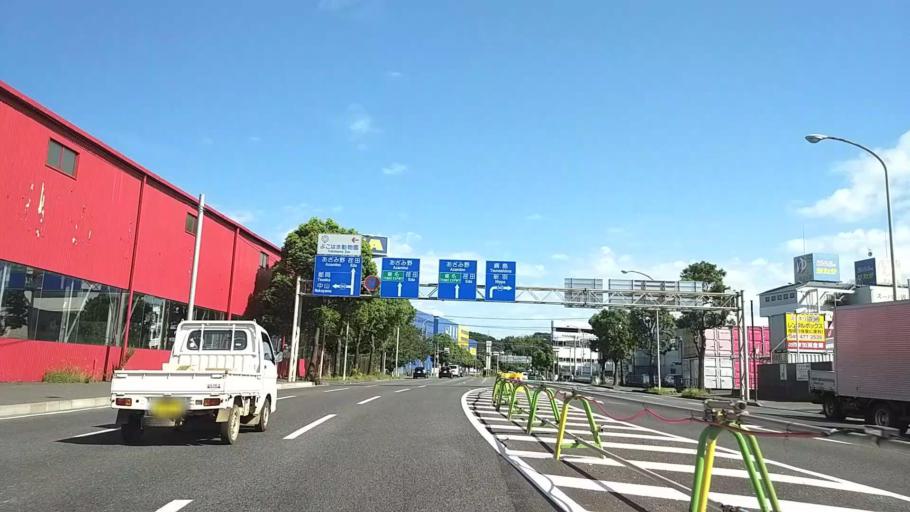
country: JP
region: Kanagawa
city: Yokohama
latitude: 35.5197
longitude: 139.5910
